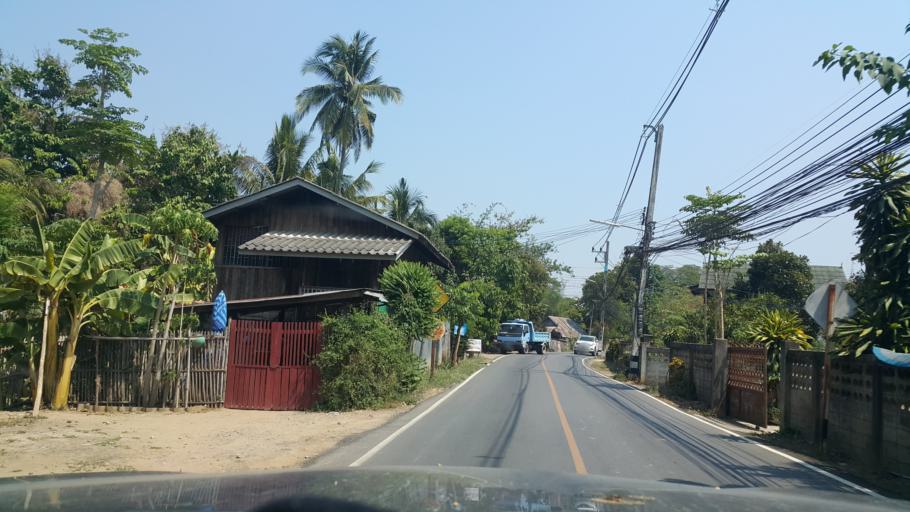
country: TH
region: Chiang Mai
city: Saraphi
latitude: 18.7267
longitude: 98.9887
